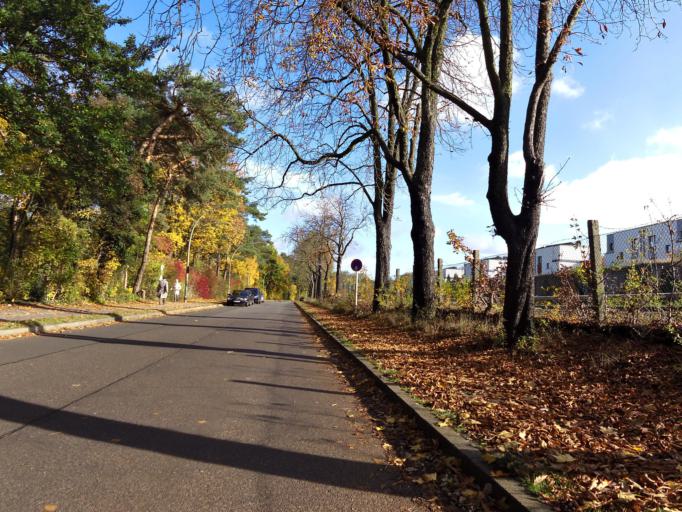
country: DE
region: Berlin
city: Nikolassee
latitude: 52.4406
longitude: 13.2168
